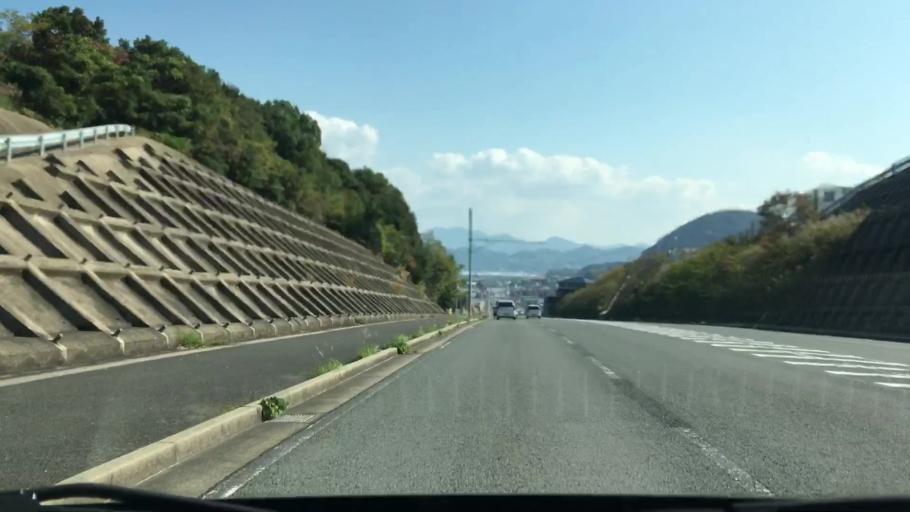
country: JP
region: Nagasaki
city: Togitsu
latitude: 32.8571
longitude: 129.8193
